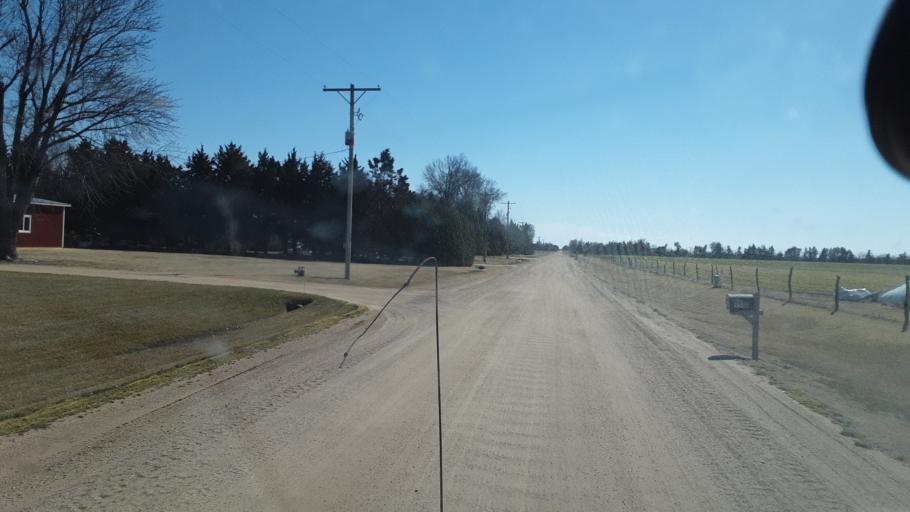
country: US
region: Kansas
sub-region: Reno County
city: South Hutchinson
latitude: 38.0115
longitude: -97.9954
